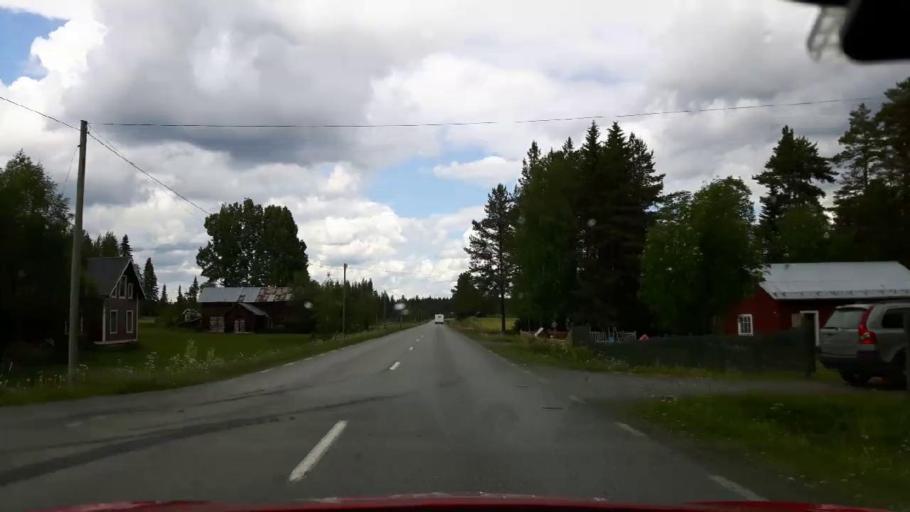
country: SE
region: Jaemtland
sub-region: Krokoms Kommun
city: Krokom
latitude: 63.5191
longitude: 14.2324
